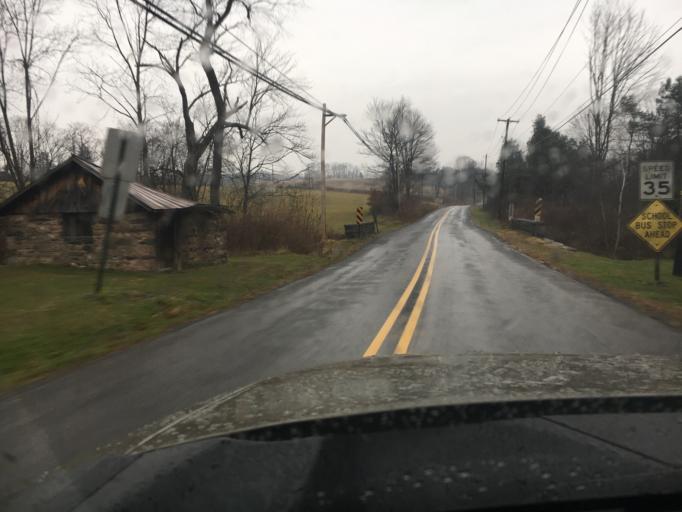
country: US
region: Pennsylvania
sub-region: Luzerne County
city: Harleigh
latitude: 41.0380
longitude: -75.9651
